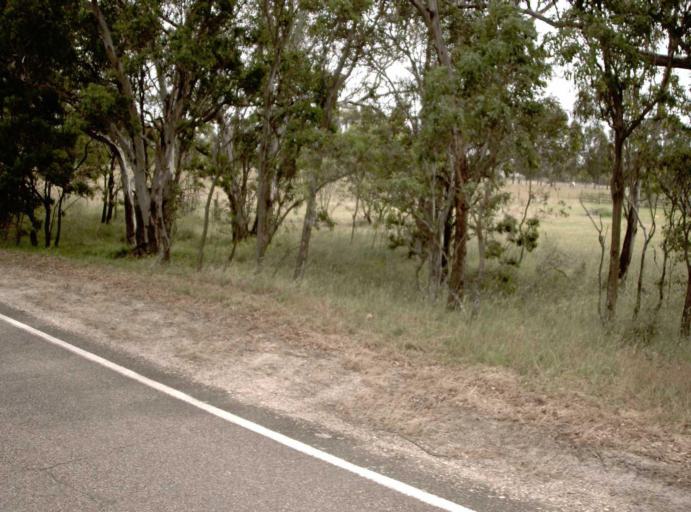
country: AU
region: Victoria
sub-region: Wellington
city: Sale
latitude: -37.9325
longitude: 147.0956
